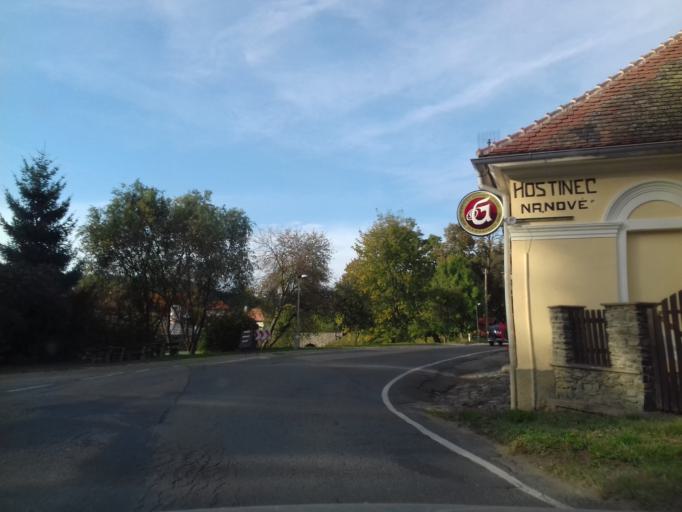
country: CZ
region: Central Bohemia
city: Neveklov
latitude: 49.7593
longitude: 14.5276
